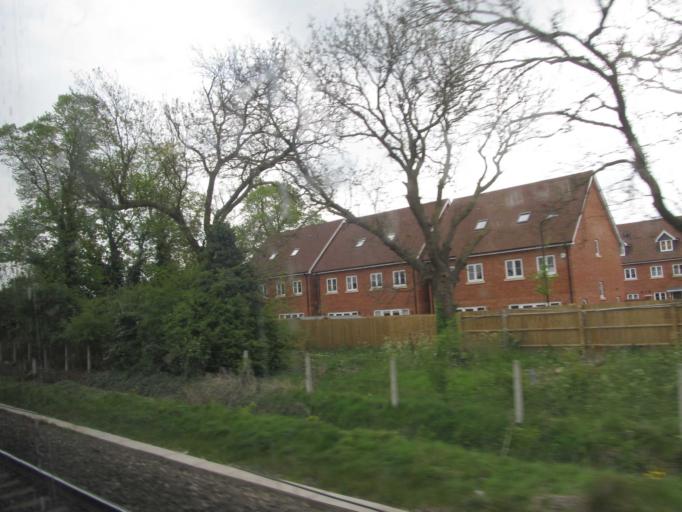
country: GB
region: England
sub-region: Slough
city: Slough
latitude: 51.5099
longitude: -0.5745
